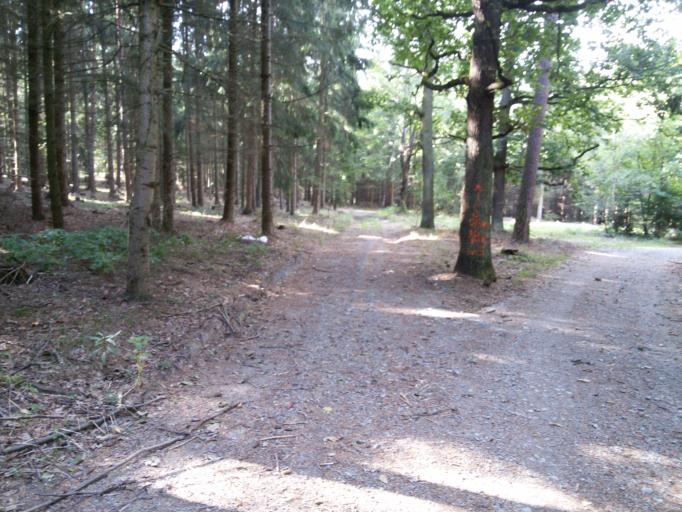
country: CZ
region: South Moravian
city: Cerna Hora
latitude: 49.3836
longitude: 16.5631
